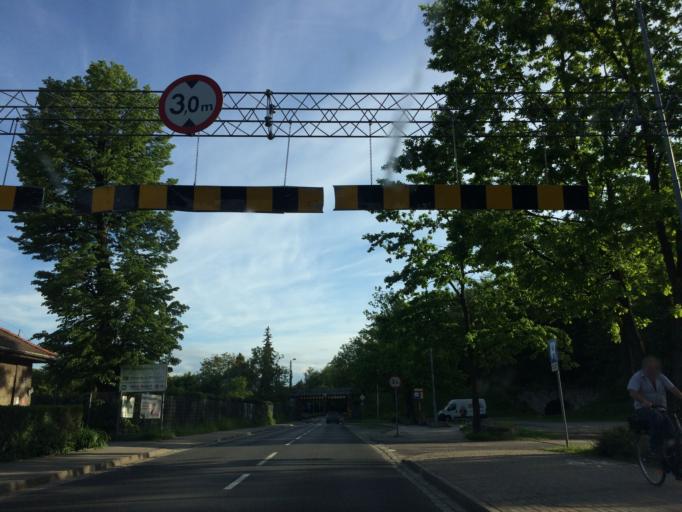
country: PL
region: Lower Silesian Voivodeship
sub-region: Powiat swidnicki
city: Swidnica
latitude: 50.8325
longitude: 16.4882
